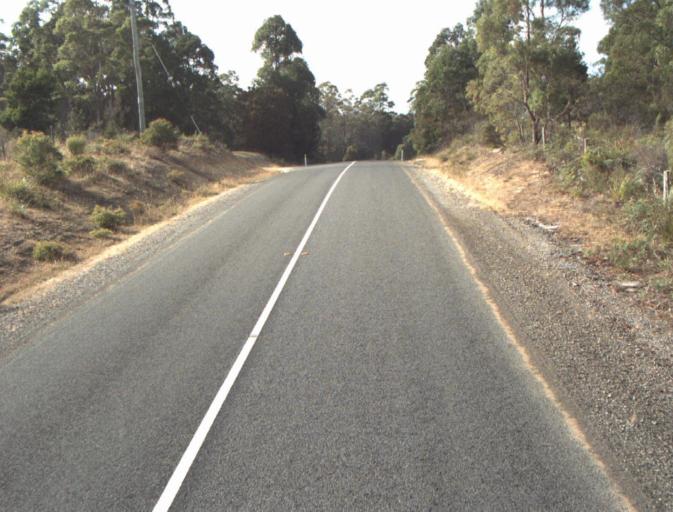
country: AU
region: Tasmania
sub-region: Dorset
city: Bridport
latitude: -41.1381
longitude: 147.2267
